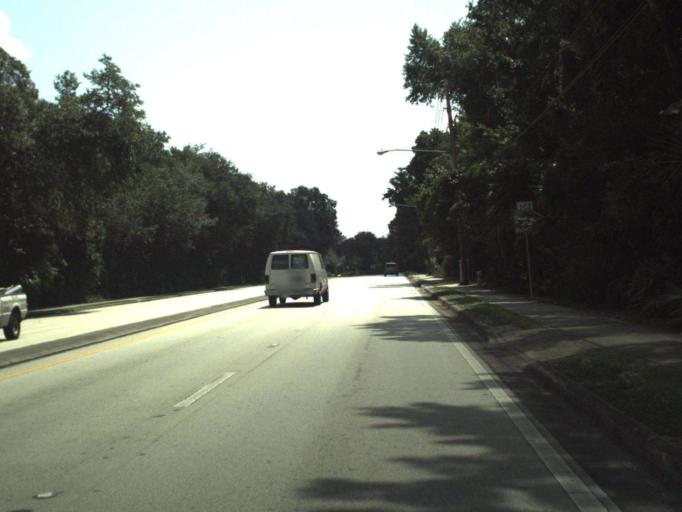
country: US
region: Florida
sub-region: Seminole County
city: Winter Springs
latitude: 28.7016
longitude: -81.2951
